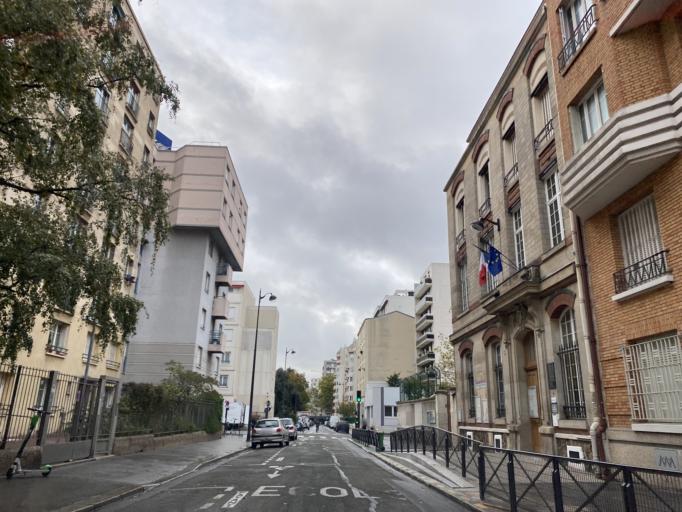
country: FR
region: Ile-de-France
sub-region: Departement de Seine-Saint-Denis
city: Le Pre-Saint-Gervais
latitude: 48.8610
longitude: 2.3830
